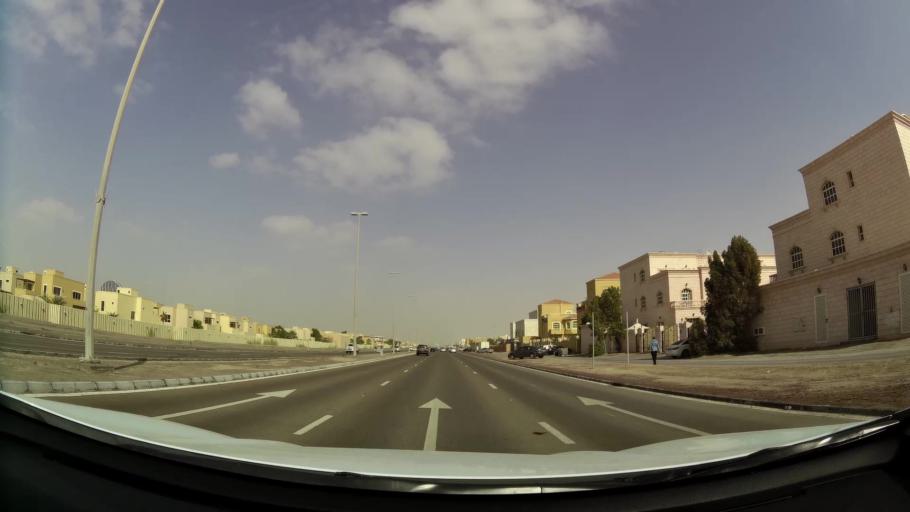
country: AE
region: Abu Dhabi
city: Abu Dhabi
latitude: 24.4312
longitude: 54.5695
